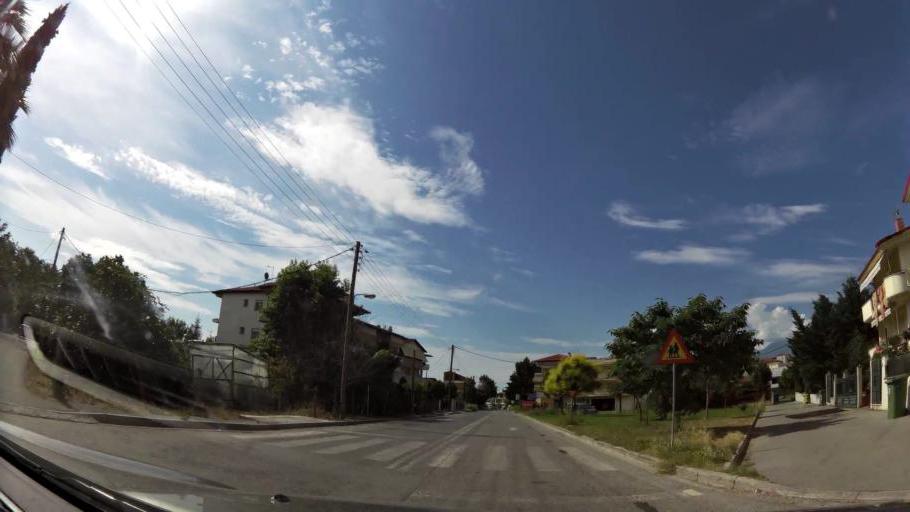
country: GR
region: Central Macedonia
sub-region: Nomos Pierias
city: Katerini
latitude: 40.2844
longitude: 22.5034
